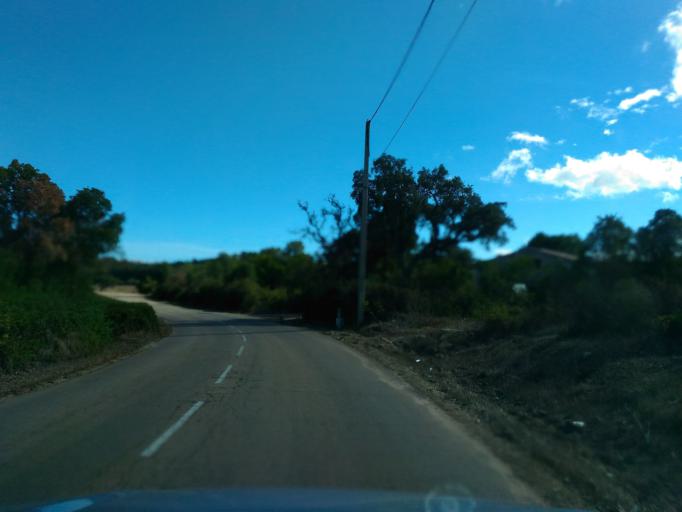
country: FR
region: Corsica
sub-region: Departement de la Corse-du-Sud
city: Porto-Vecchio
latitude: 41.6953
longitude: 9.3609
